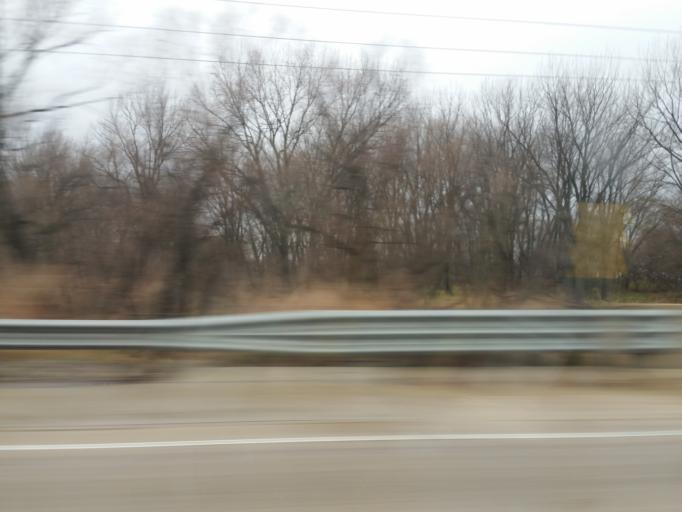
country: US
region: Iowa
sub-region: Black Hawk County
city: Elk Run Heights
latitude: 42.4062
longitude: -92.2621
